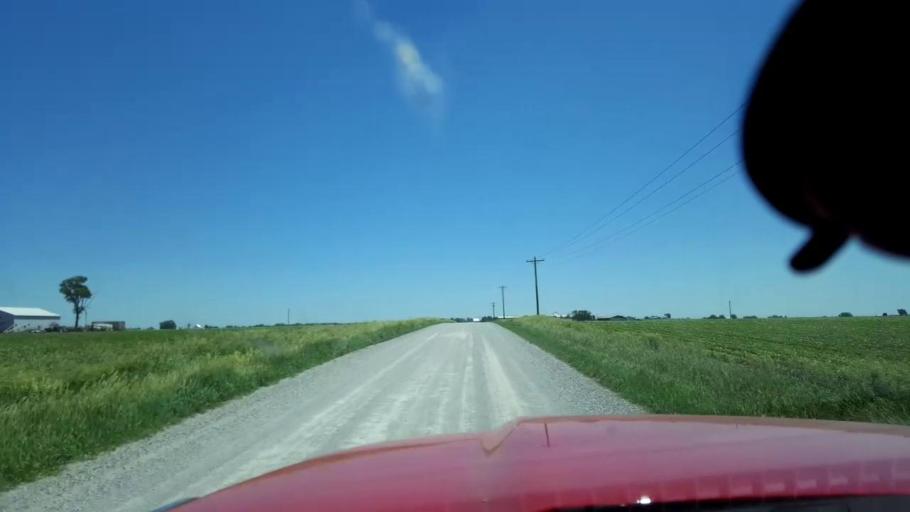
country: US
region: Iowa
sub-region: Washington County
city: Washington
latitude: 41.2799
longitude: -91.6475
